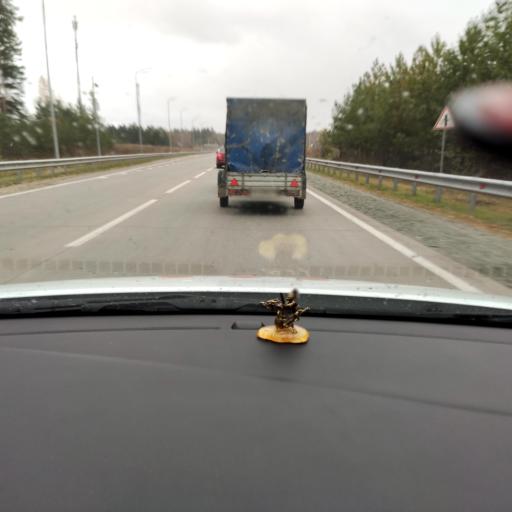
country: RU
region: Tatarstan
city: Stolbishchi
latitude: 55.6425
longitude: 49.1196
